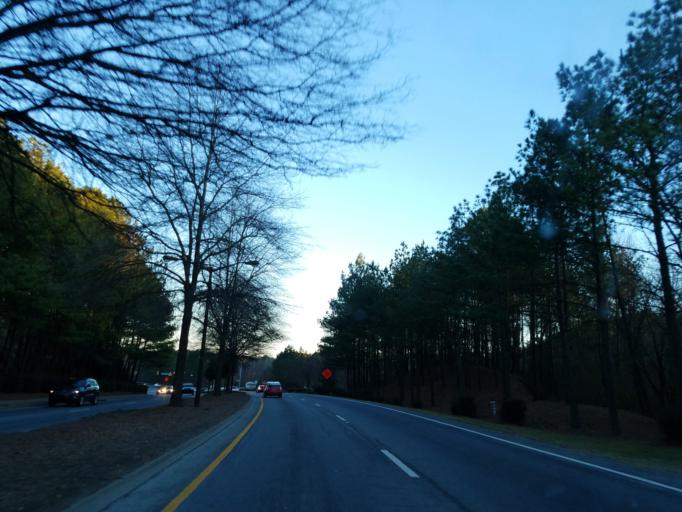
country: US
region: Georgia
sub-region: Cherokee County
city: Woodstock
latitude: 34.1029
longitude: -84.5384
